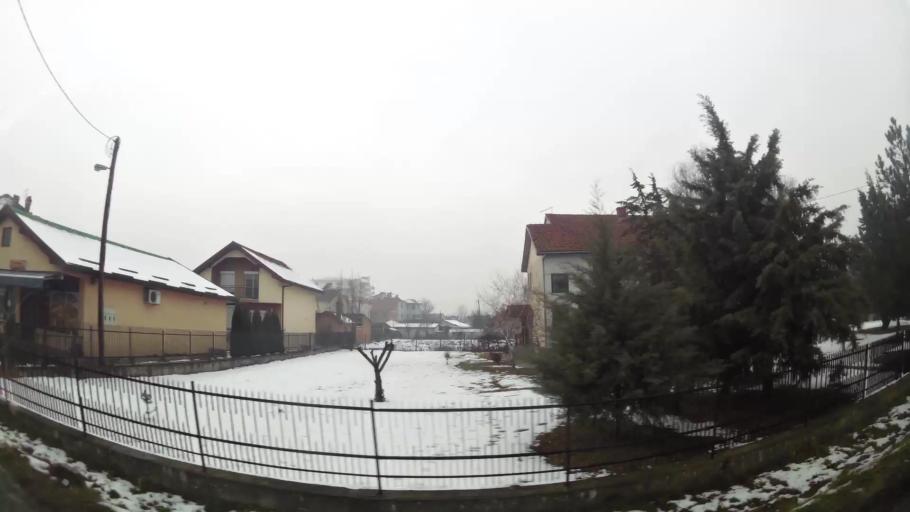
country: MK
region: Petrovec
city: Petrovec
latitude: 41.9382
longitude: 21.6184
